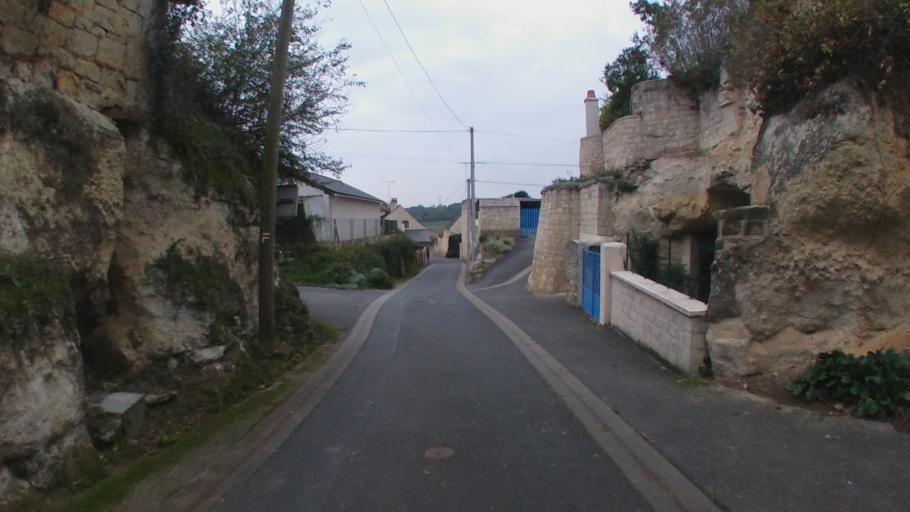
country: FR
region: Pays de la Loire
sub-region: Departement de Maine-et-Loire
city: Distre
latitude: 47.2416
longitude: -0.1376
